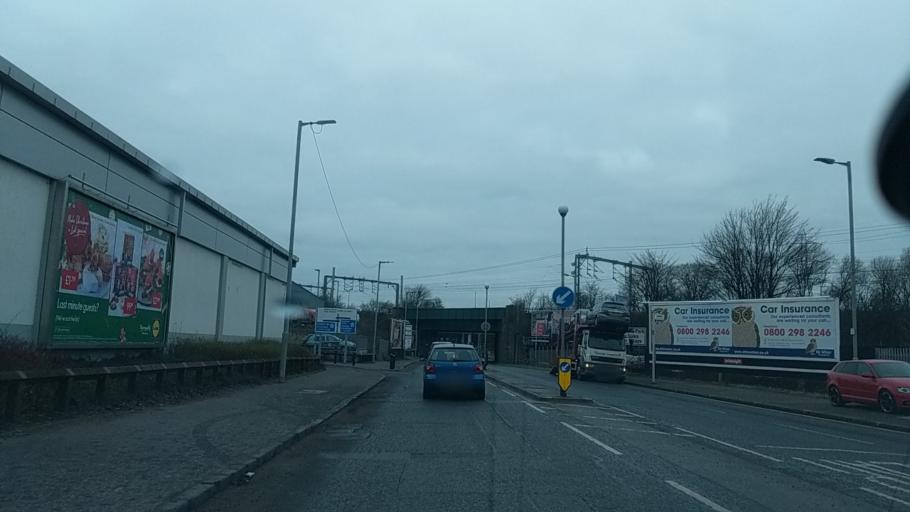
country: GB
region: Scotland
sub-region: South Lanarkshire
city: Rutherglen
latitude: 55.8275
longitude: -4.1948
